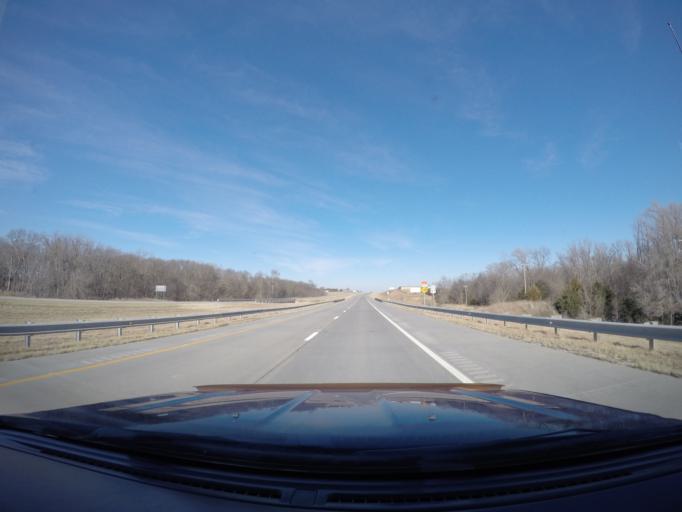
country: US
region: Kansas
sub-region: Cloud County
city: Concordia
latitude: 39.6980
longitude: -97.6600
